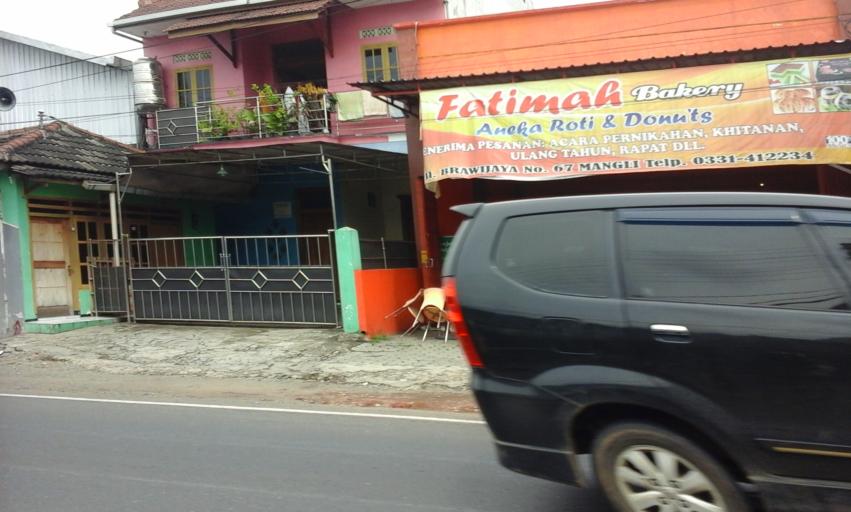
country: ID
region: East Java
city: Mangli
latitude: -8.1908
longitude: 113.6499
